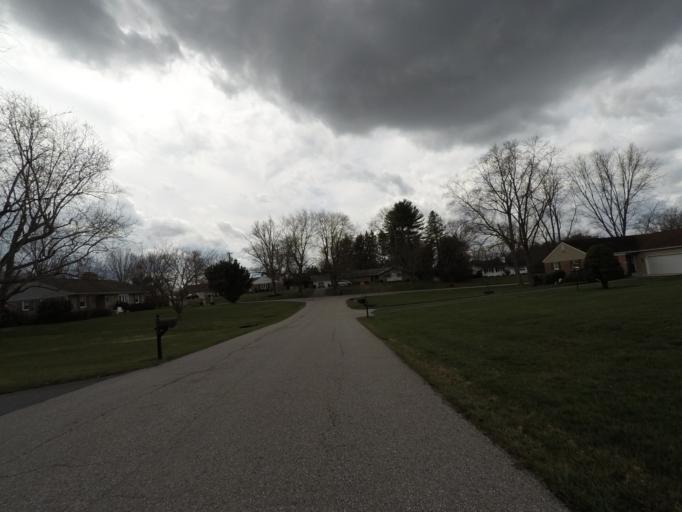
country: US
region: Maryland
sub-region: Howard County
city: Columbia
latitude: 39.2580
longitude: -76.8270
